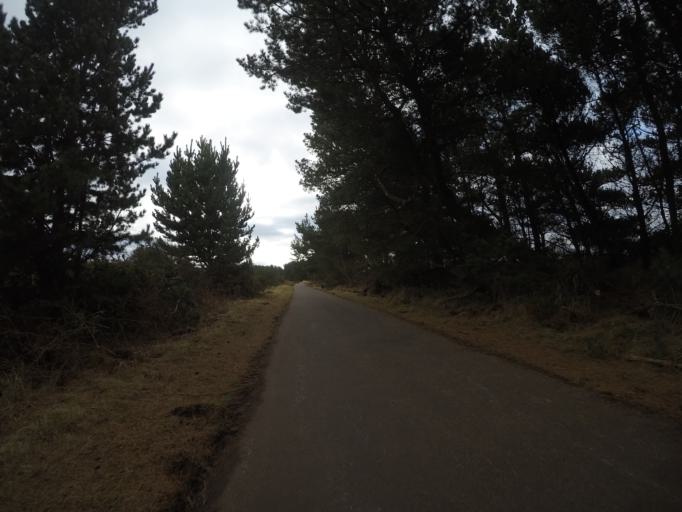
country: GB
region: Scotland
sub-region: North Ayrshire
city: Irvine
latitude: 55.5959
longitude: -4.6744
